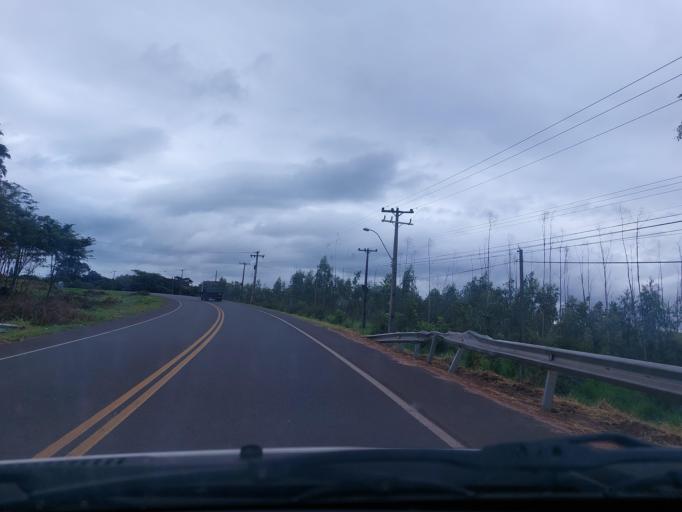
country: PY
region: San Pedro
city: Guayaybi
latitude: -24.6661
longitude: -56.4128
